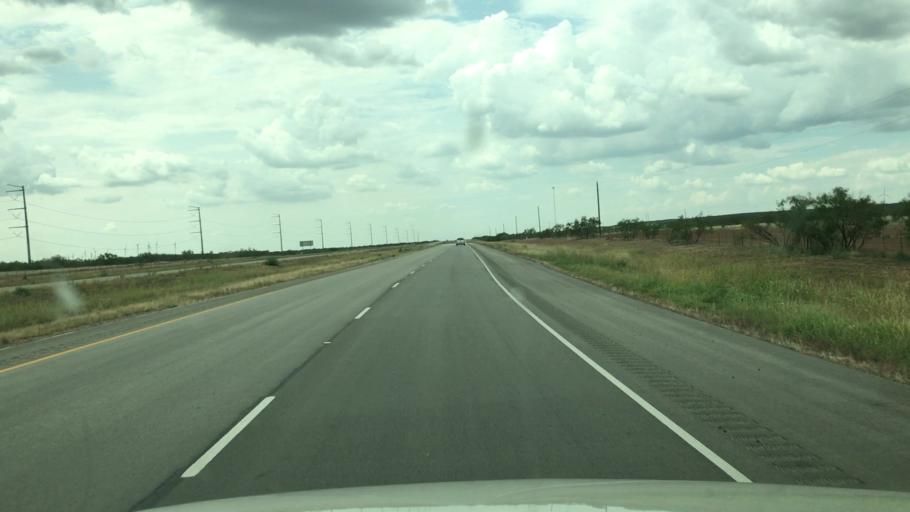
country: US
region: Texas
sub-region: Glasscock County
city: Garden City
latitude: 31.9697
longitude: -101.2405
